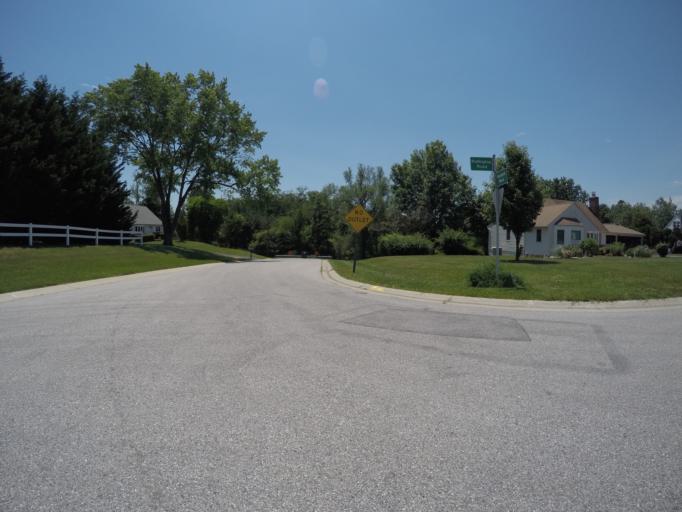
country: US
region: Maryland
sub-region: Howard County
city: Ilchester
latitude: 39.2353
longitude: -76.7870
